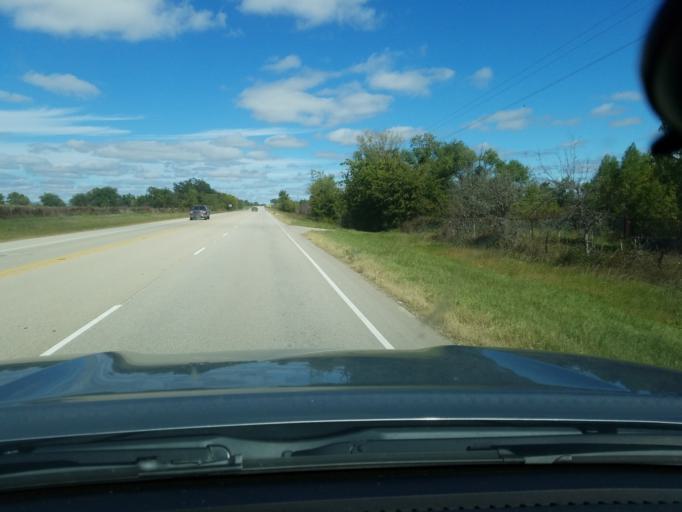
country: US
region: Texas
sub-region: Hamilton County
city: Hamilton
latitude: 31.6515
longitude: -98.1457
